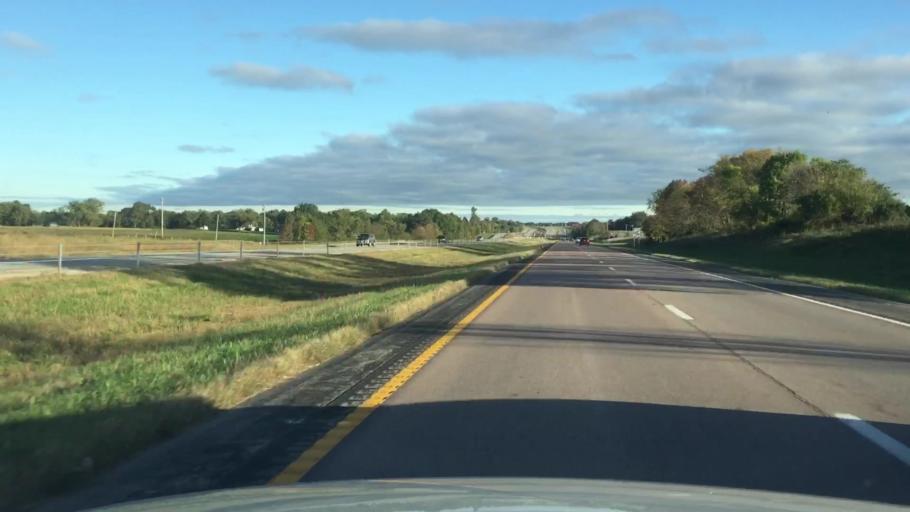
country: US
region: Missouri
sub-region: Boone County
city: Ashland
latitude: 38.8414
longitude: -92.2491
